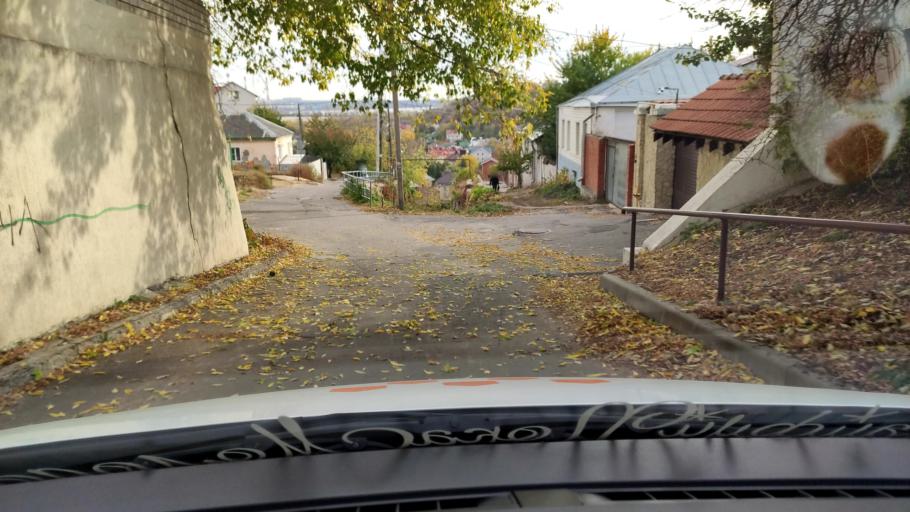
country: RU
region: Voronezj
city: Voronezh
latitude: 51.6544
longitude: 39.2068
